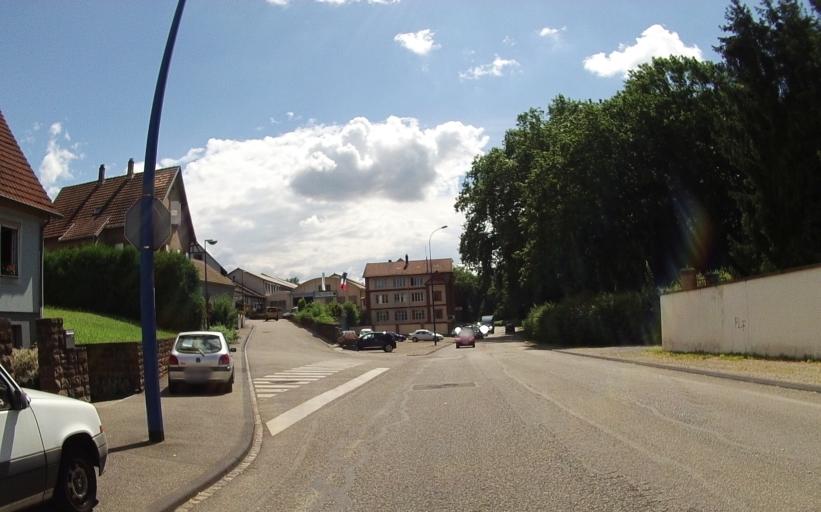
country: FR
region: Alsace
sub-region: Departement du Bas-Rhin
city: Reichshoffen
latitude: 48.9288
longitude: 7.6682
